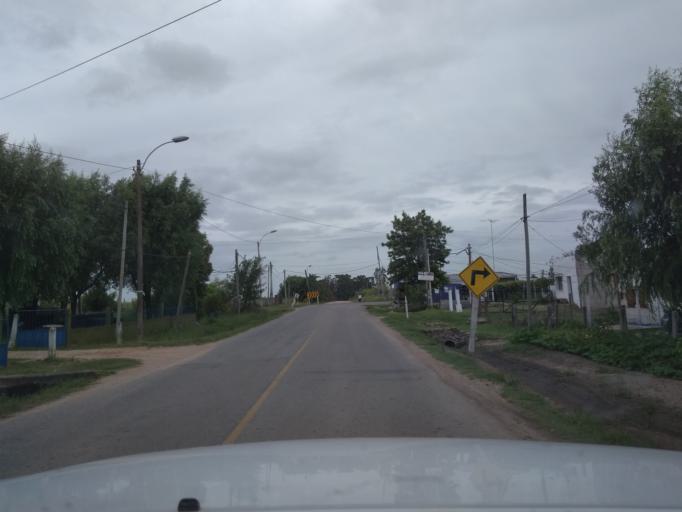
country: UY
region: Canelones
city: Tala
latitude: -34.3474
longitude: -55.7600
